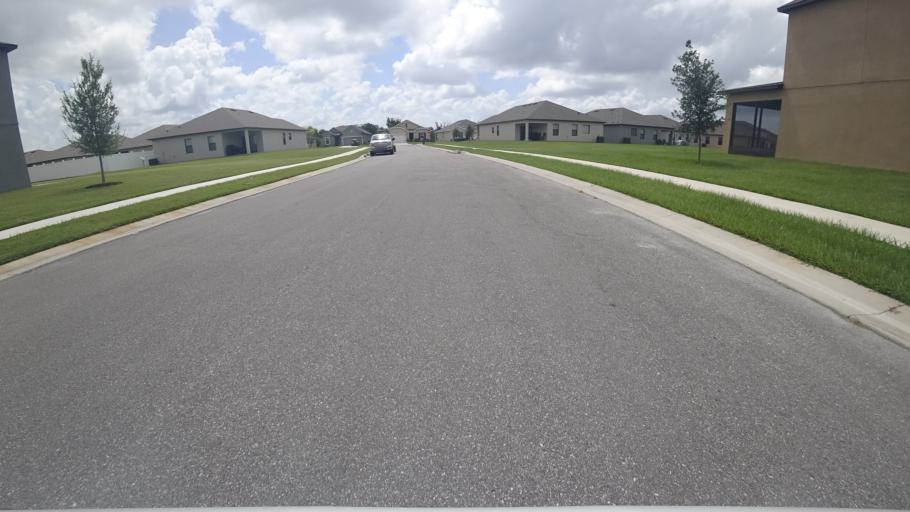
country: US
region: Florida
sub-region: Manatee County
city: Ellenton
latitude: 27.5494
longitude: -82.5225
